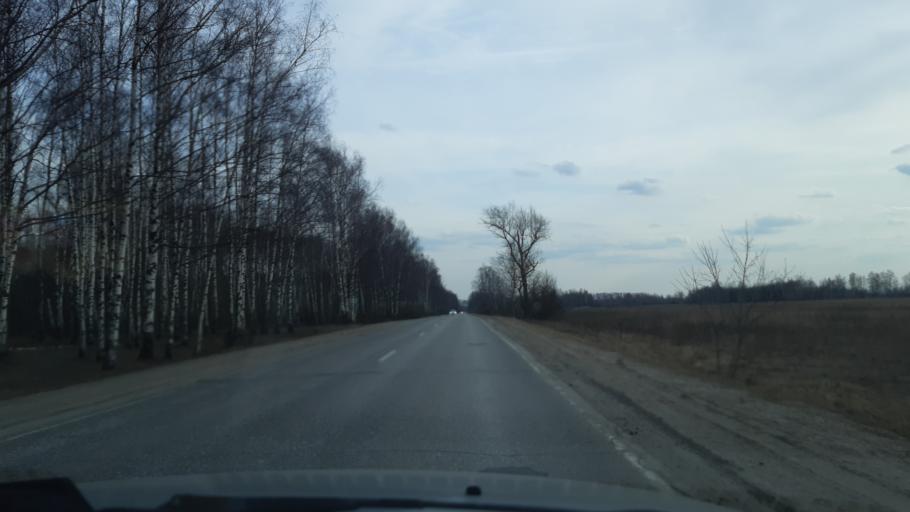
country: RU
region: Vladimir
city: Luknovo
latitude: 56.2344
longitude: 42.0342
